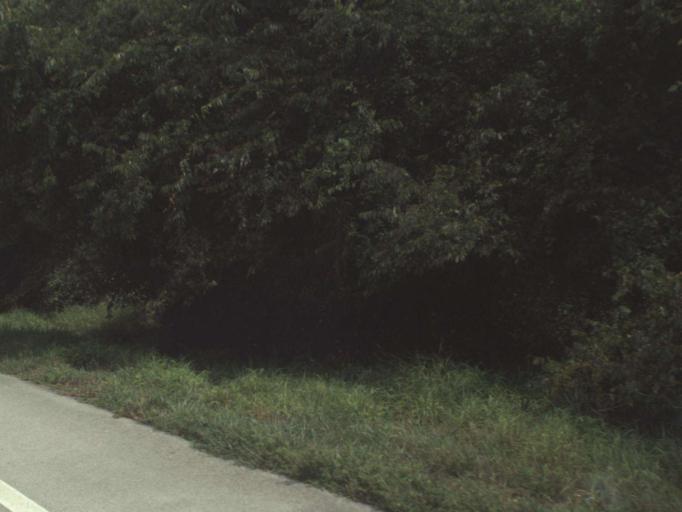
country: US
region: Florida
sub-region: Martin County
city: Indiantown
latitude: 27.0289
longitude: -80.6337
